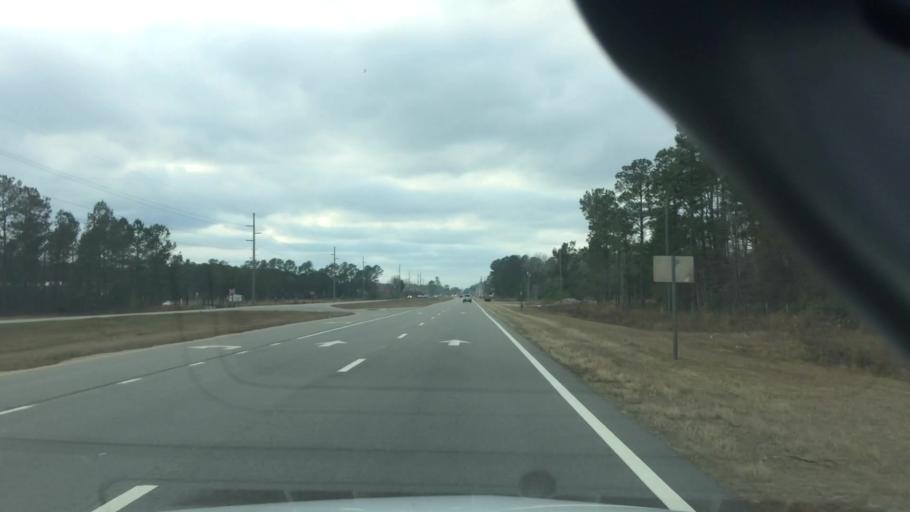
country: US
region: North Carolina
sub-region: Brunswick County
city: Carolina Shores
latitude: 33.9401
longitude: -78.5458
